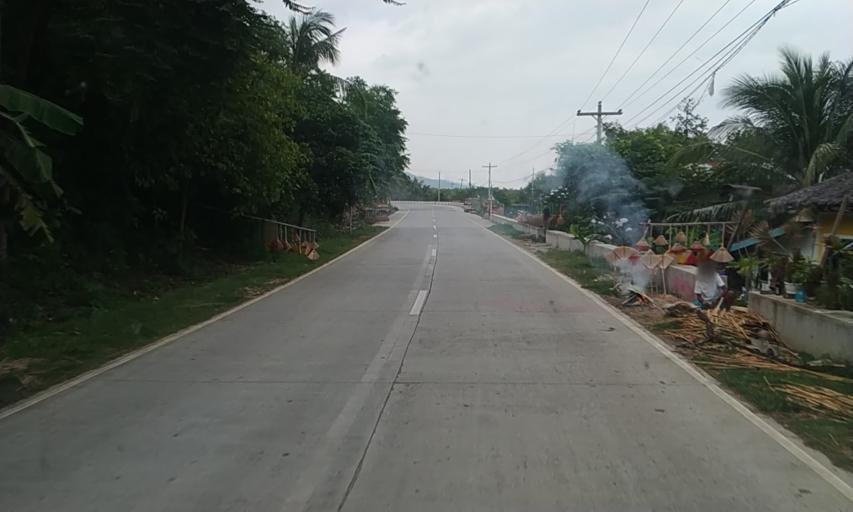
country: PH
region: Central Visayas
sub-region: Province of Negros Oriental
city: Calamba
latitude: 10.1988
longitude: 123.2986
